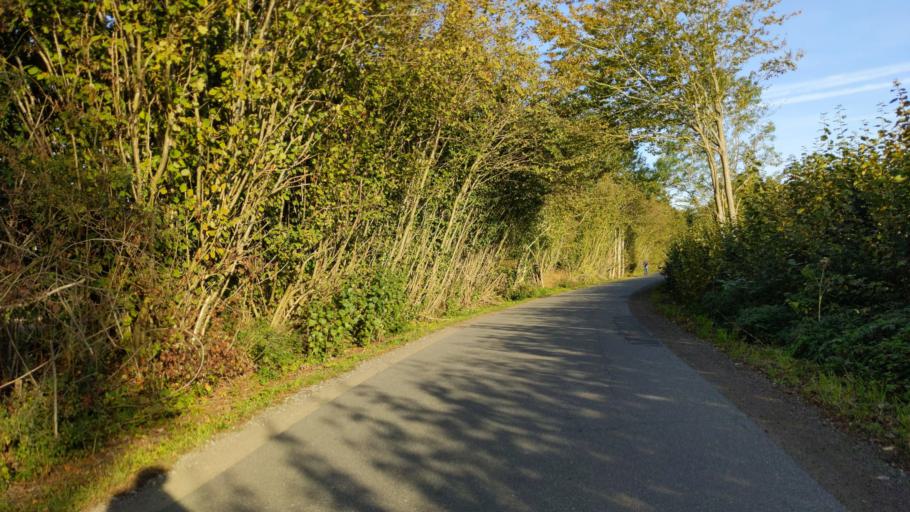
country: DE
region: Schleswig-Holstein
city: Susel
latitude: 54.0872
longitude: 10.6593
